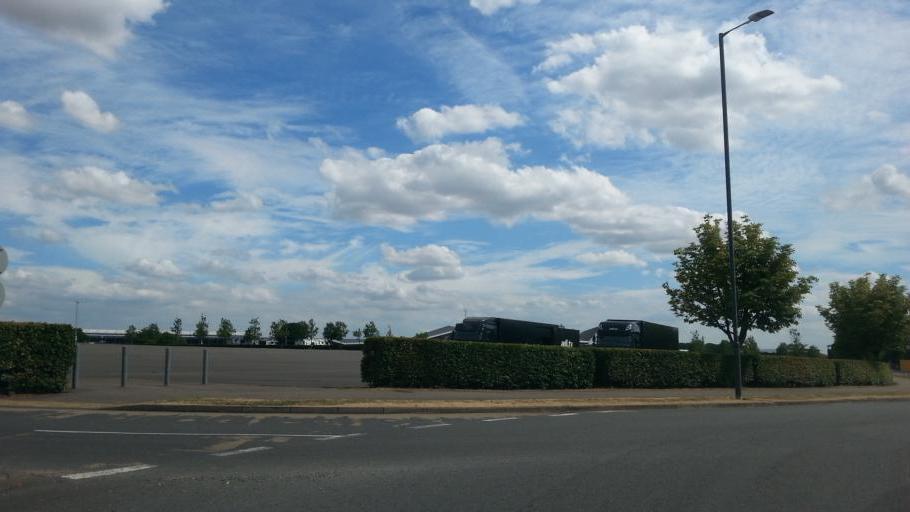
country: GB
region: England
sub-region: Northamptonshire
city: Silverstone
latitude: 52.0734
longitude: -1.0256
